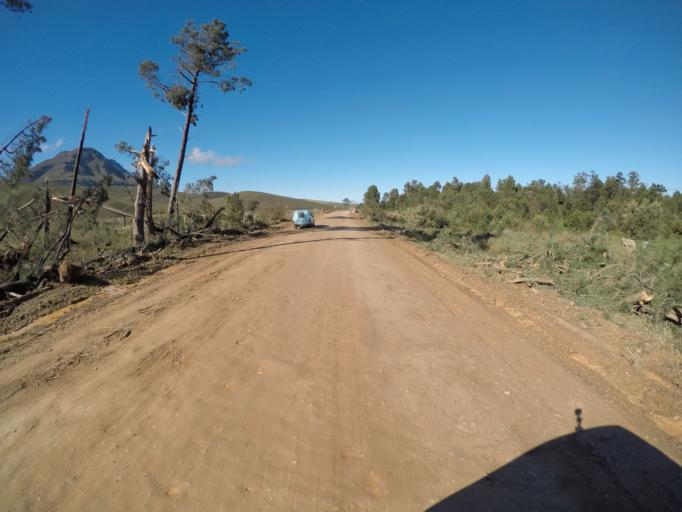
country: ZA
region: Western Cape
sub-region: Overberg District Municipality
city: Caledon
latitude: -34.0528
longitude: 19.6132
